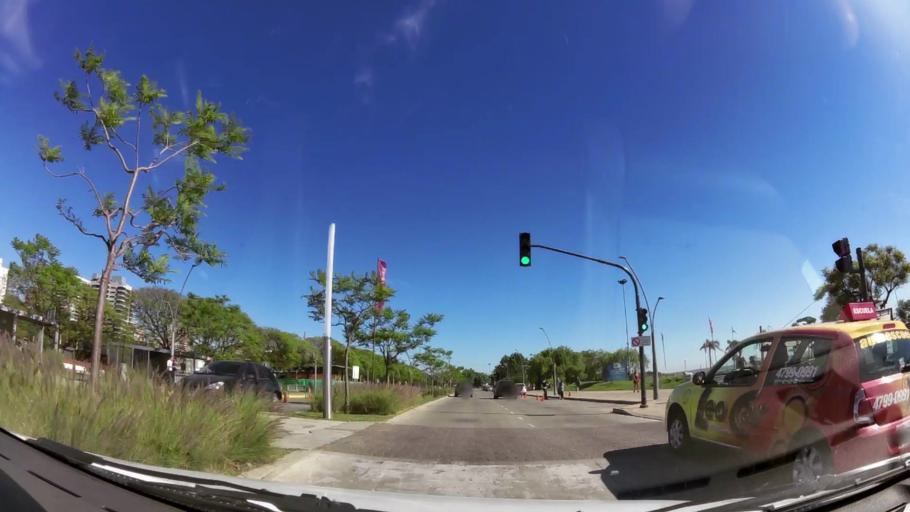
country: AR
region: Buenos Aires
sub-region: Partido de Vicente Lopez
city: Olivos
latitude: -34.5226
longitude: -58.4689
